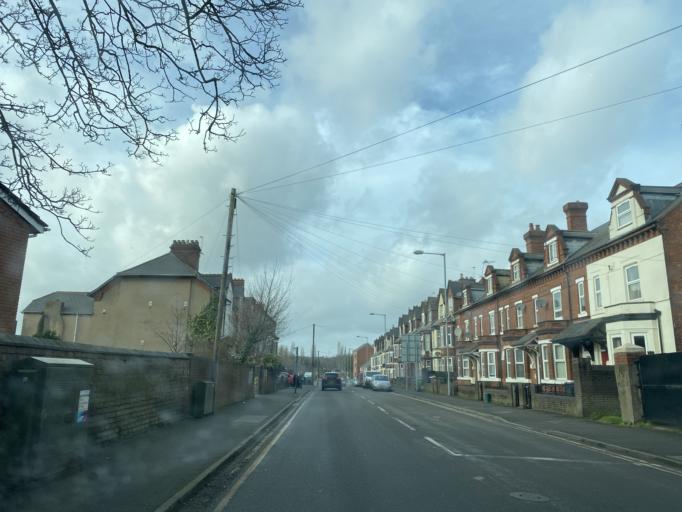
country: GB
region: England
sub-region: Walsall
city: Walsall
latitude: 52.5780
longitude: -1.9873
